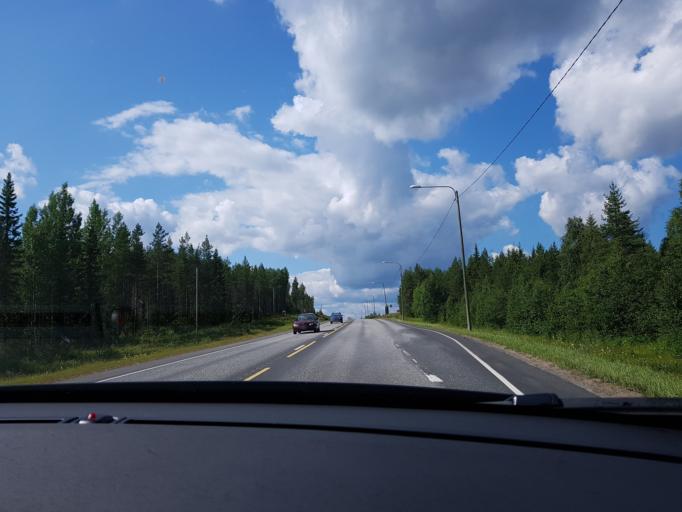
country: FI
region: Kainuu
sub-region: Kajaani
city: Paltamo
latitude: 64.3215
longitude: 28.0521
